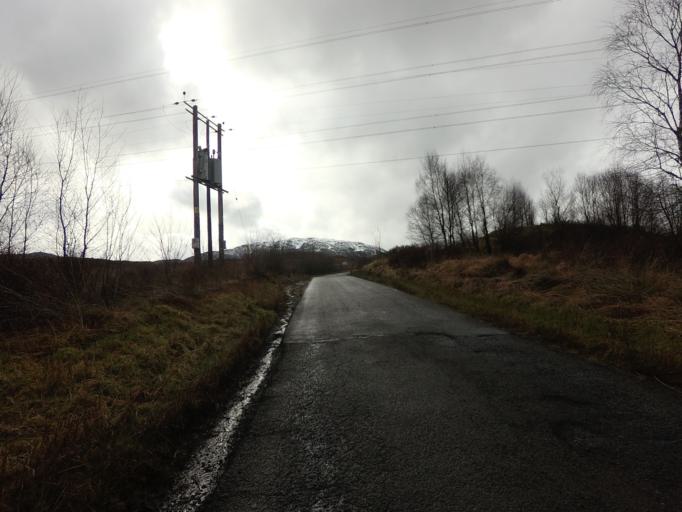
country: GB
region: Scotland
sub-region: West Dunbartonshire
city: Balloch
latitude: 56.2557
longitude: -4.5841
